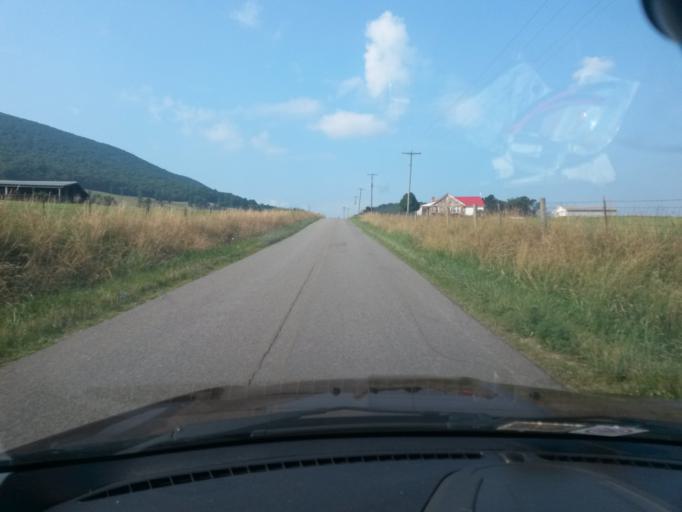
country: US
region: Virginia
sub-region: Giles County
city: Narrows
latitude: 37.3814
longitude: -80.7919
